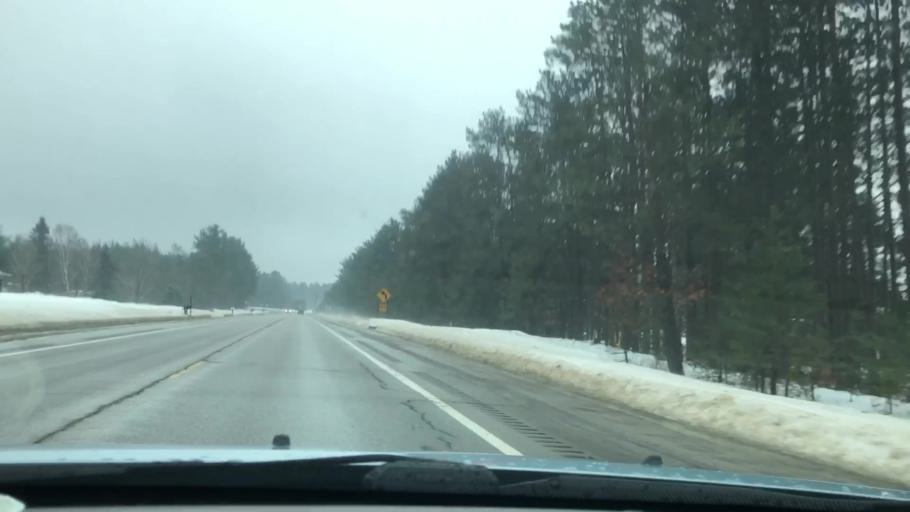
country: US
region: Michigan
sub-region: Otsego County
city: Gaylord
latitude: 45.0341
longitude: -84.7759
